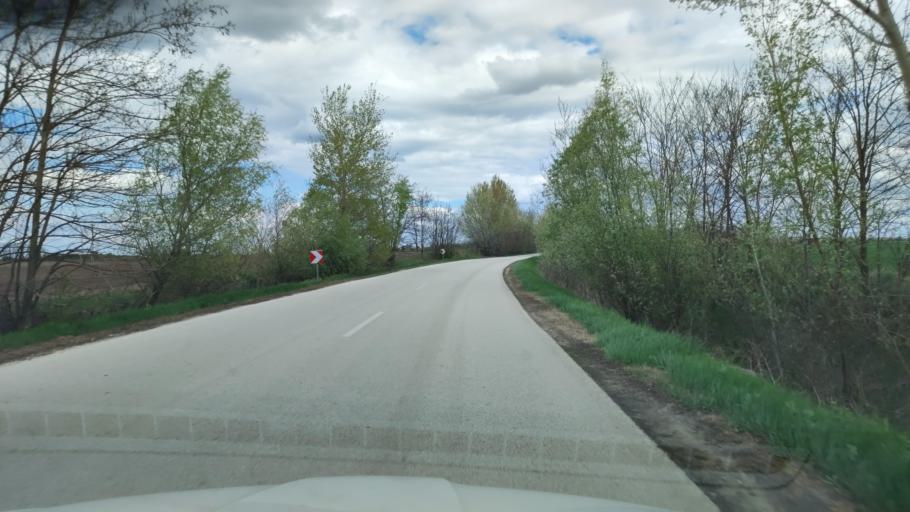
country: HU
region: Pest
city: Jaszkarajeno
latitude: 47.0844
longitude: 20.0150
